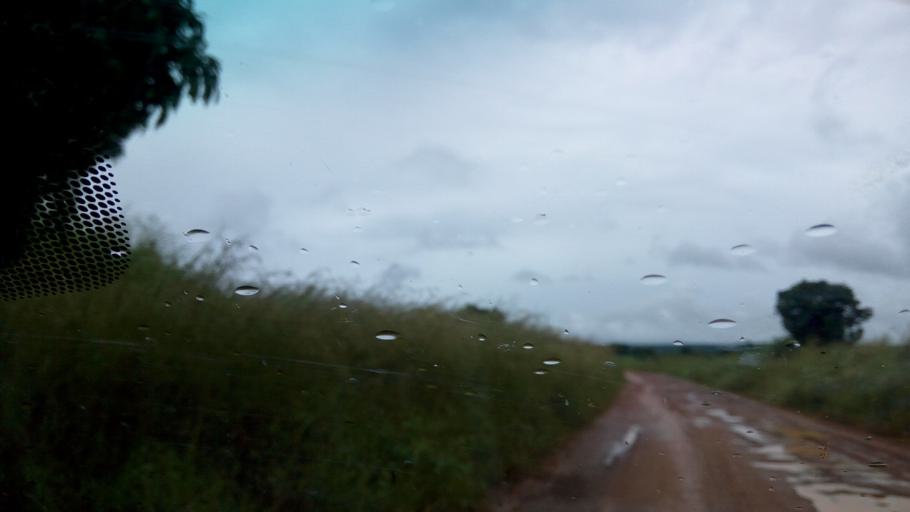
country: ZM
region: Luapula
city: Nchelenge
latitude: -9.1250
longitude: 28.3032
